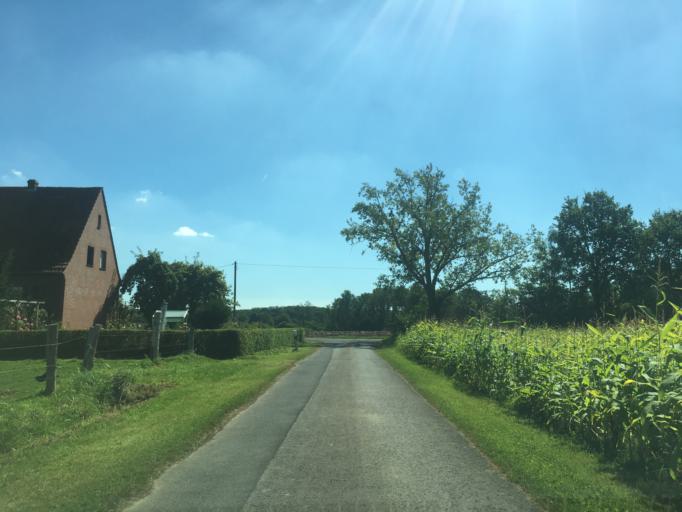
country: DE
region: North Rhine-Westphalia
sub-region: Regierungsbezirk Munster
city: Altenberge
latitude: 52.0314
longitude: 7.5351
